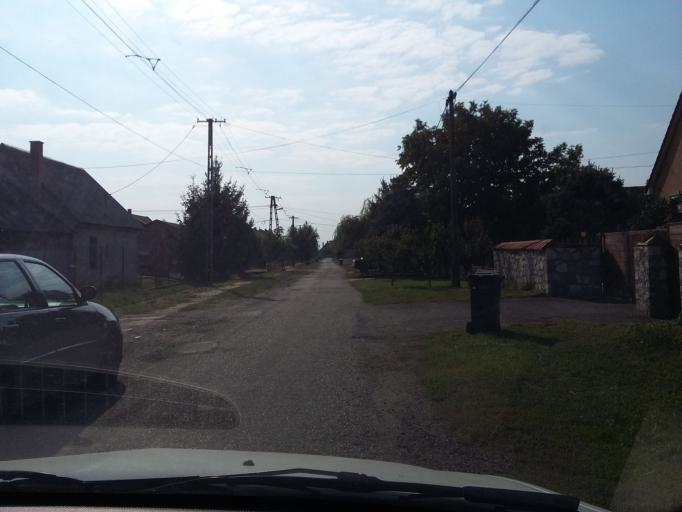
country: HU
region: Borsod-Abauj-Zemplen
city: Bekecs
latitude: 48.1516
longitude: 21.1781
